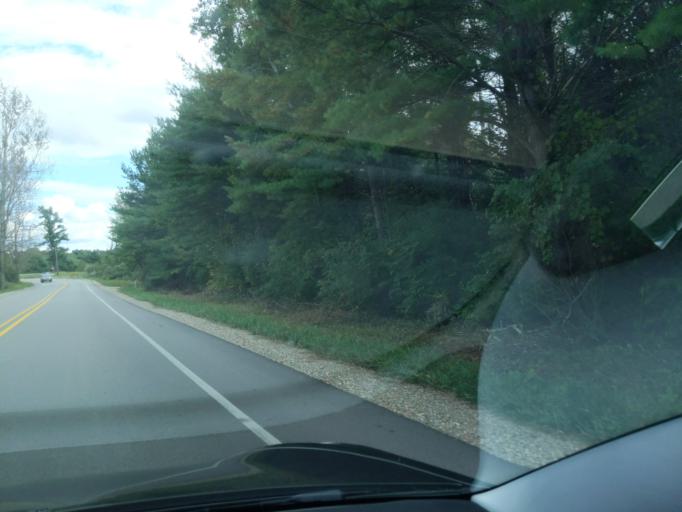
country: US
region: Michigan
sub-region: Kalkaska County
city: Rapid City
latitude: 44.8943
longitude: -85.2741
